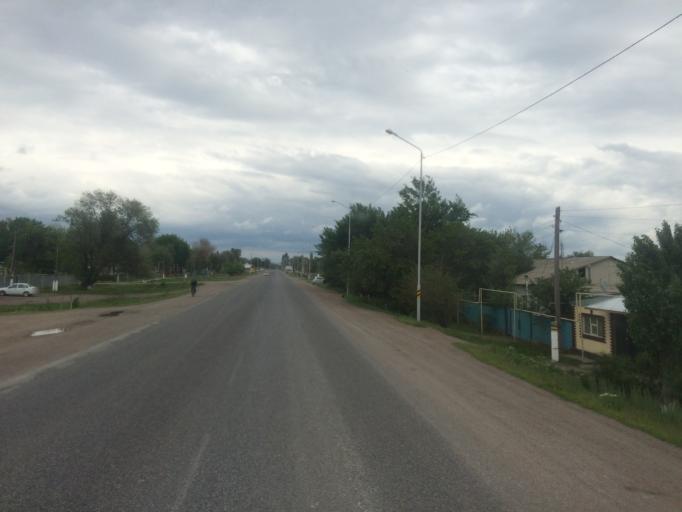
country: KZ
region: Zhambyl
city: Georgiyevka
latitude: 43.2280
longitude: 74.3870
